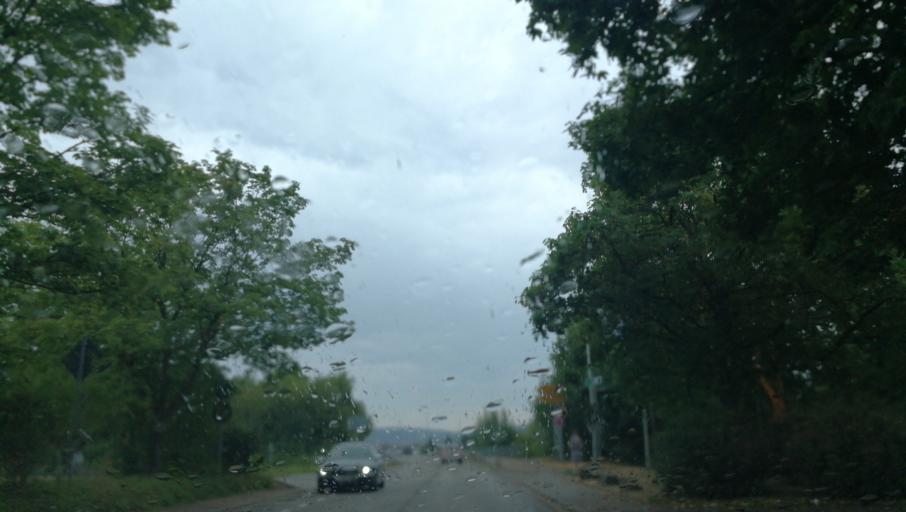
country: DE
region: Saarland
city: Losheim
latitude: 49.5197
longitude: 6.7415
